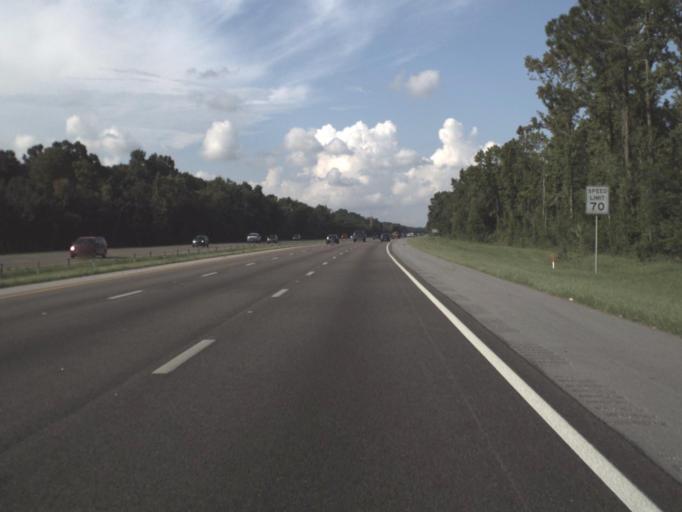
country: US
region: Florida
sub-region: Hillsborough County
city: Lutz
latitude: 28.1387
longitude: -82.4118
